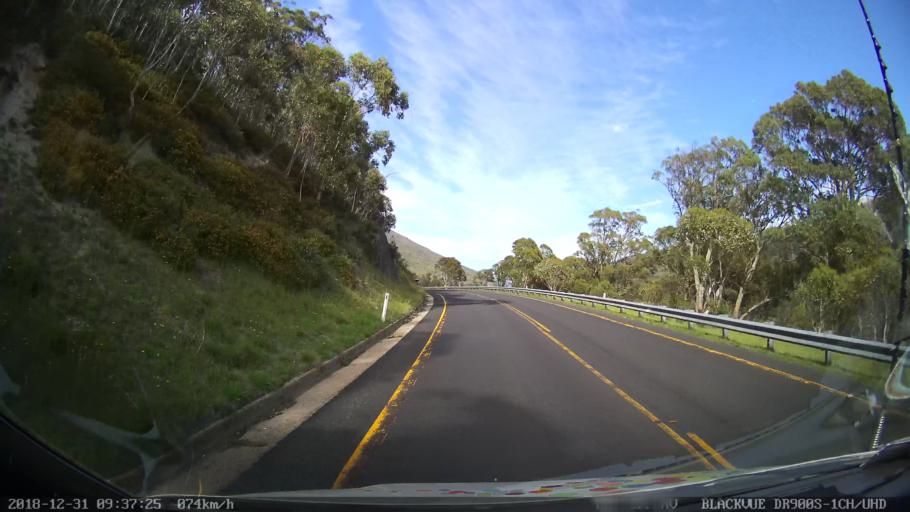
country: AU
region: New South Wales
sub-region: Snowy River
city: Jindabyne
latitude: -36.4662
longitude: 148.3760
